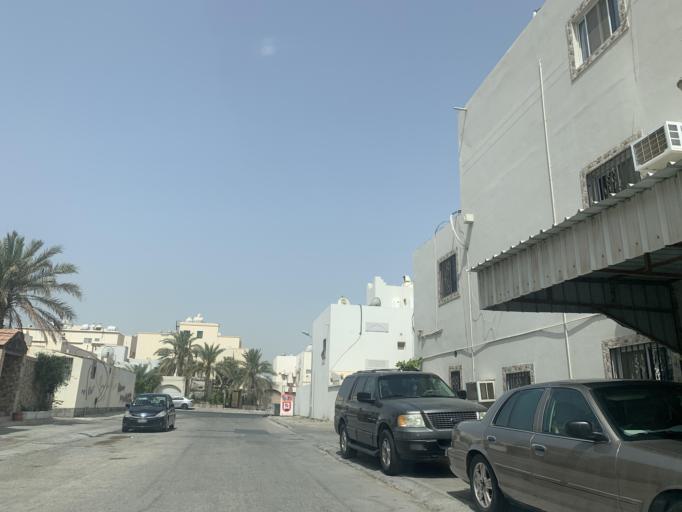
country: BH
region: Northern
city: Madinat `Isa
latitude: 26.1516
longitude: 50.5198
